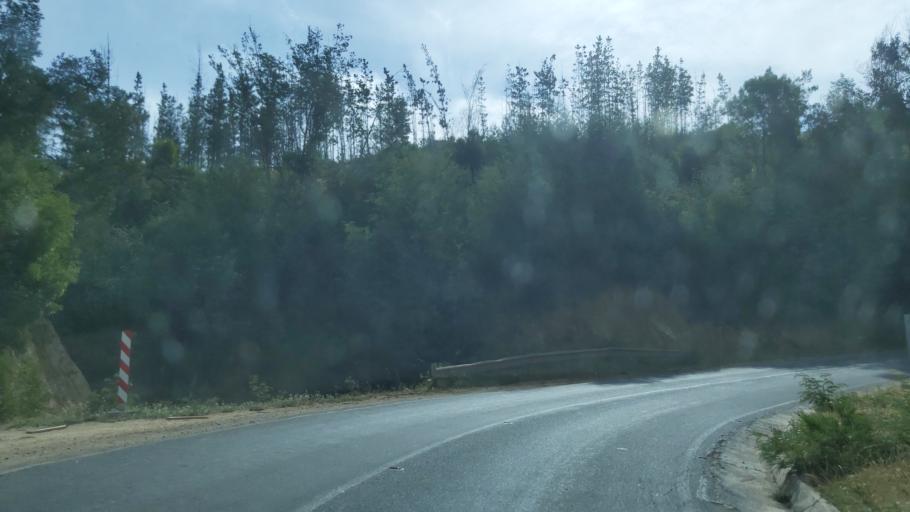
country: CL
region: Maule
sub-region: Provincia de Talca
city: Constitucion
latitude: -34.8550
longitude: -72.0306
